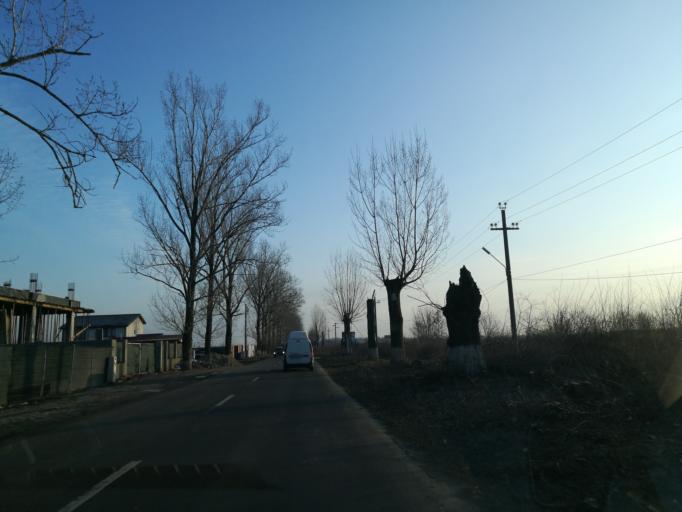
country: RO
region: Ilfov
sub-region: Comuna Balotesti
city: Balotesti
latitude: 44.6246
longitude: 26.1431
